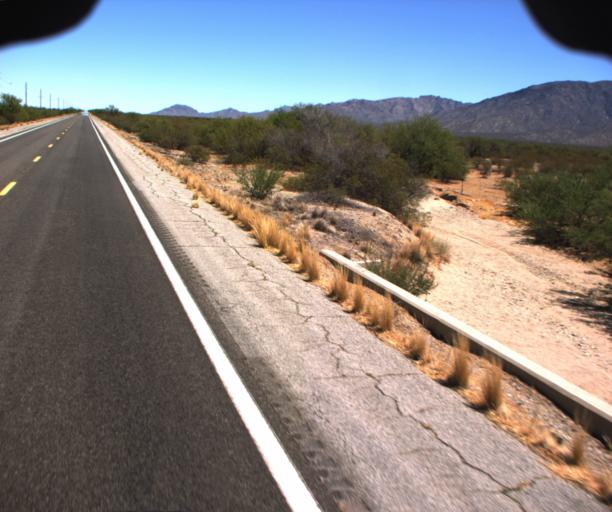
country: US
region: Arizona
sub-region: La Paz County
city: Salome
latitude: 33.8535
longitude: -113.4415
